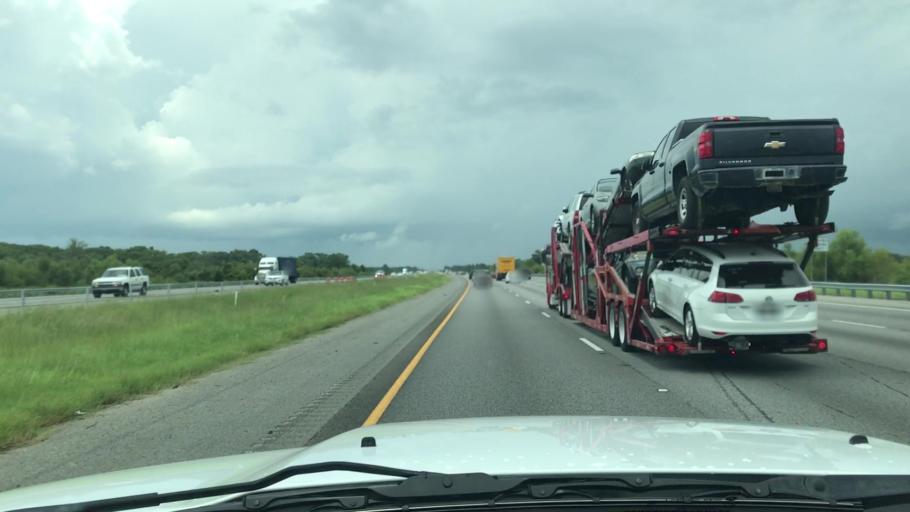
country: US
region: Georgia
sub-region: McIntosh County
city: Darien
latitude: 31.3453
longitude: -81.4627
